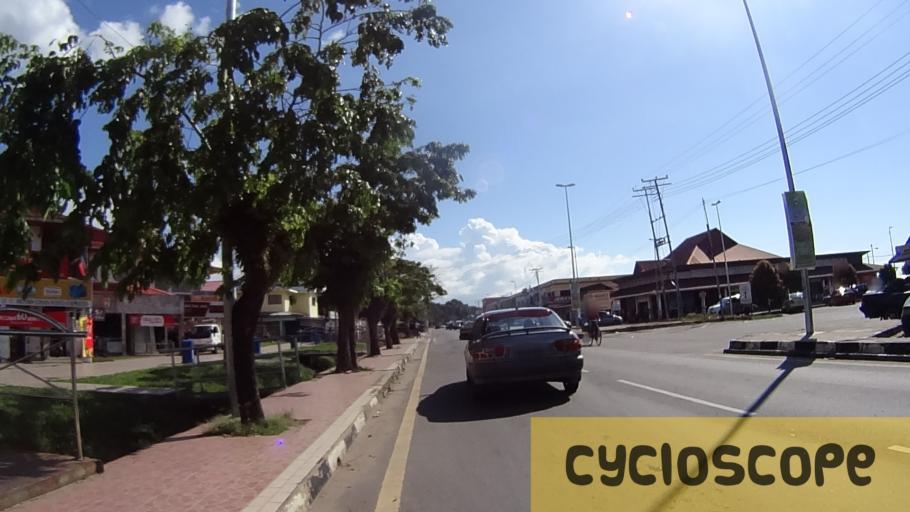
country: MY
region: Sabah
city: Beaufort
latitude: 5.0768
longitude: 115.5494
